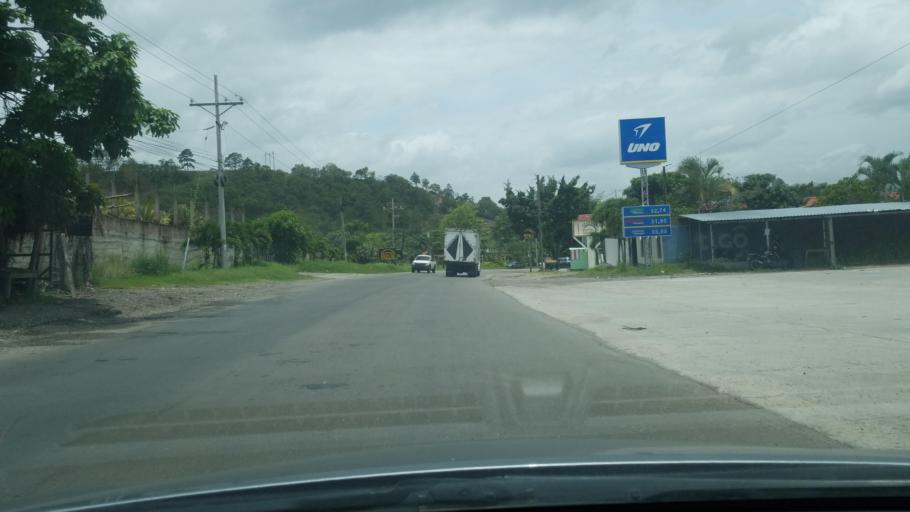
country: HN
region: Copan
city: Cucuyagua
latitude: 14.6673
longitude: -88.8663
